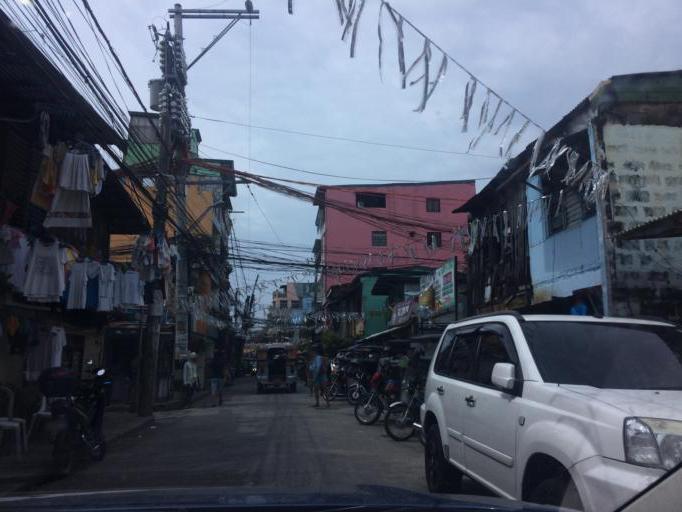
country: PH
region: Metro Manila
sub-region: Makati City
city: Makati City
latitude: 14.5459
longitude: 121.0026
